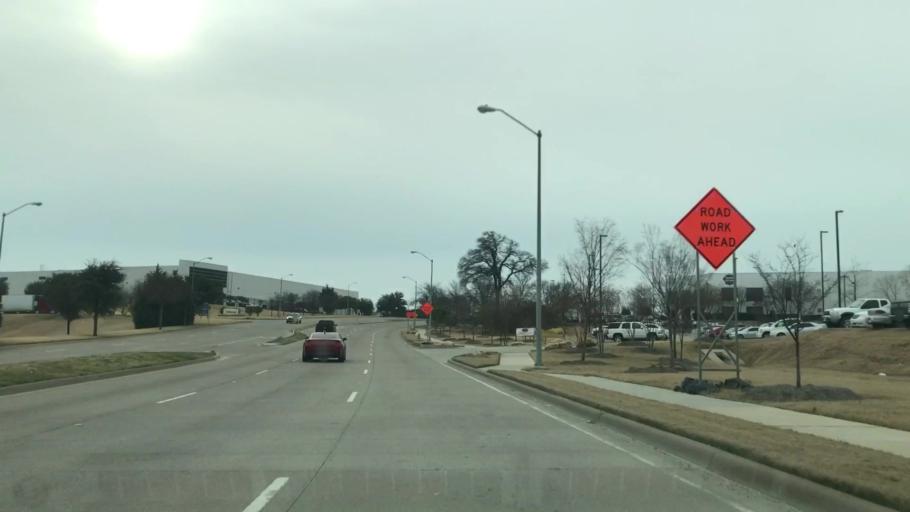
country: US
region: Texas
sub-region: Dallas County
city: Cockrell Hill
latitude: 32.7530
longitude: -96.8926
